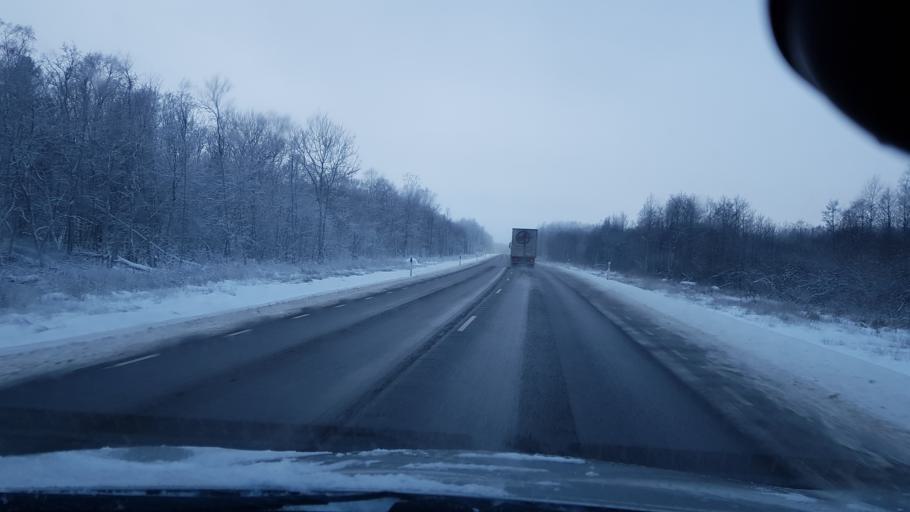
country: EE
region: Harju
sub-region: Paldiski linn
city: Paldiski
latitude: 59.3402
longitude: 24.1425
